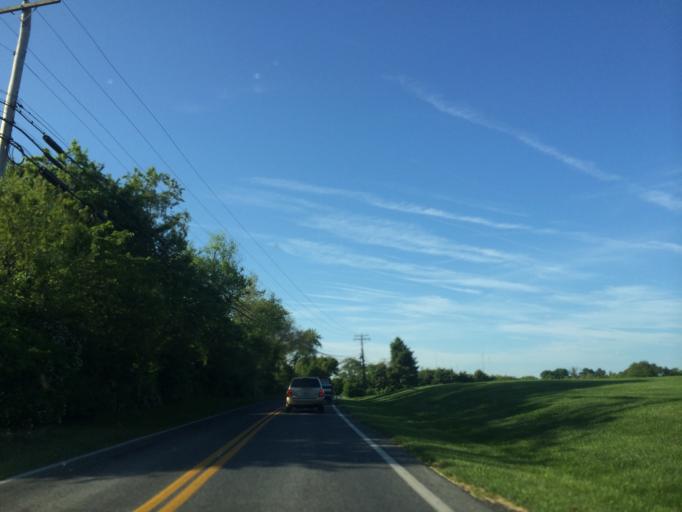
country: US
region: Maryland
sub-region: Carroll County
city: Sykesville
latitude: 39.2959
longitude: -77.0121
